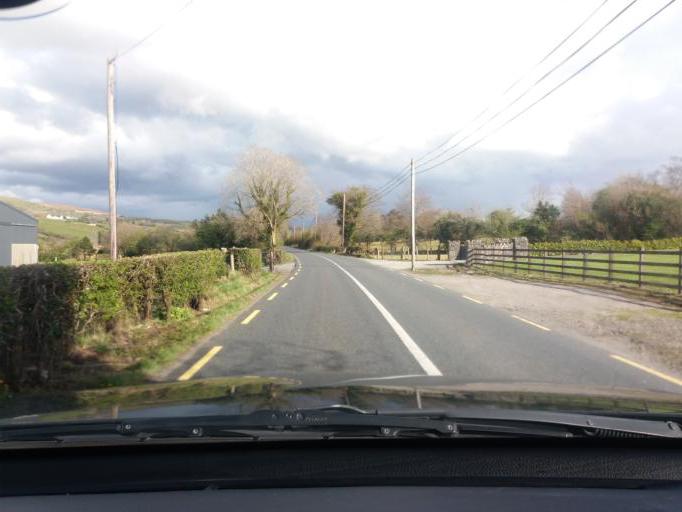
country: IE
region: Connaught
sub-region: County Leitrim
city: Manorhamilton
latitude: 54.3429
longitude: -8.2310
